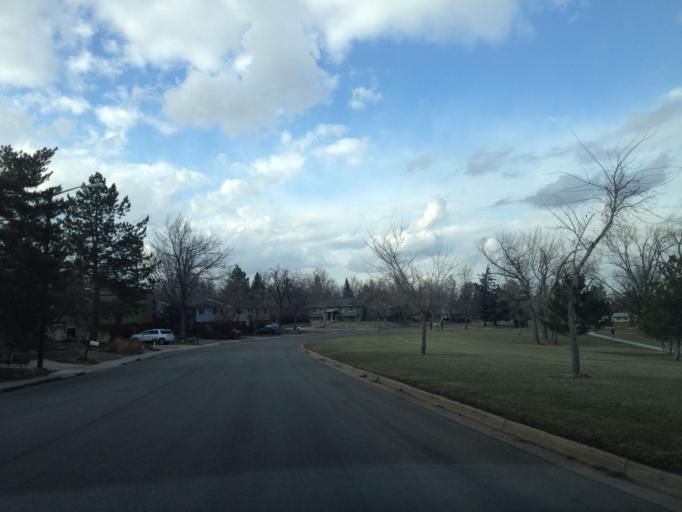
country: US
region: Colorado
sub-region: Boulder County
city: Boulder
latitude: 39.9715
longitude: -105.2522
